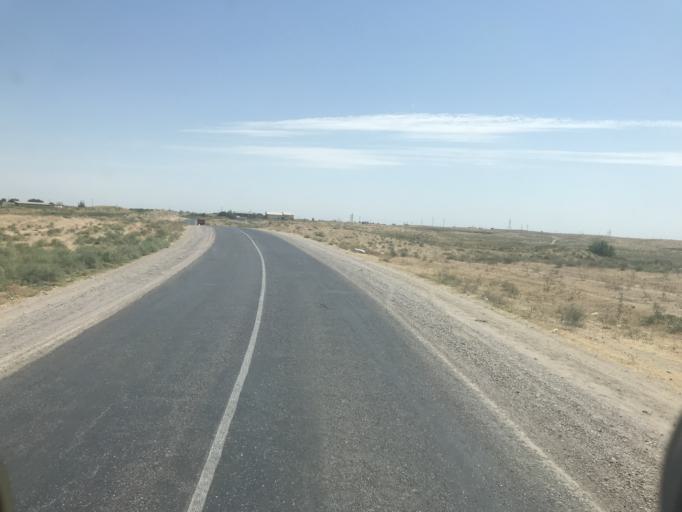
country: UZ
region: Toshkent
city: Yangiyul
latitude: 41.3381
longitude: 68.8799
